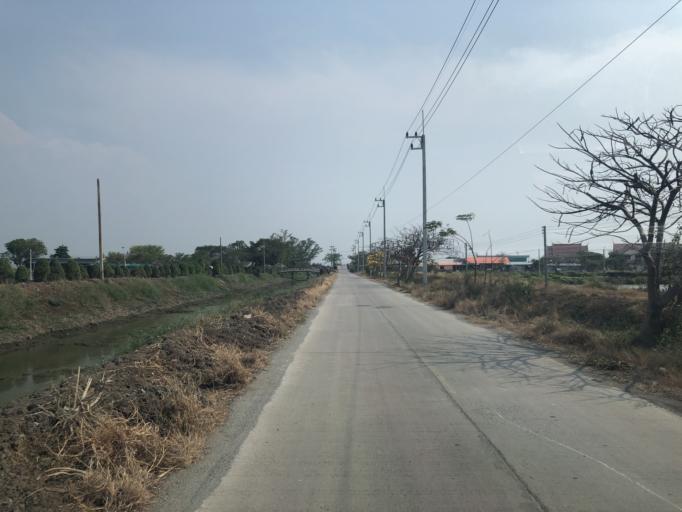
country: TH
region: Samut Prakan
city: Bang Bo
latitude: 13.5342
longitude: 100.9032
